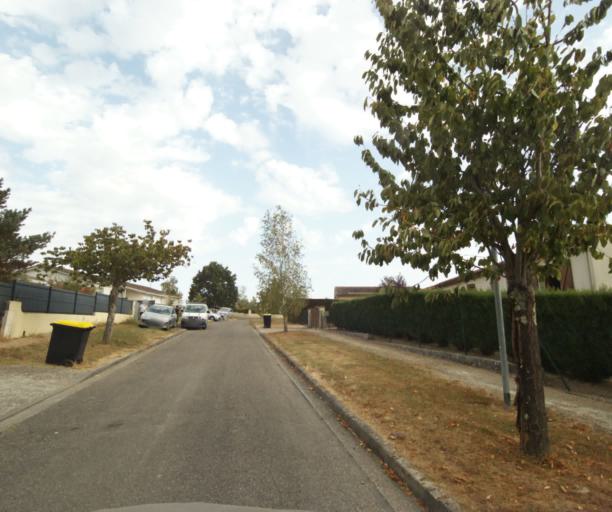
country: FR
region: Aquitaine
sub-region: Departement de la Gironde
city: Creon
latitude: 44.7681
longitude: -0.3464
